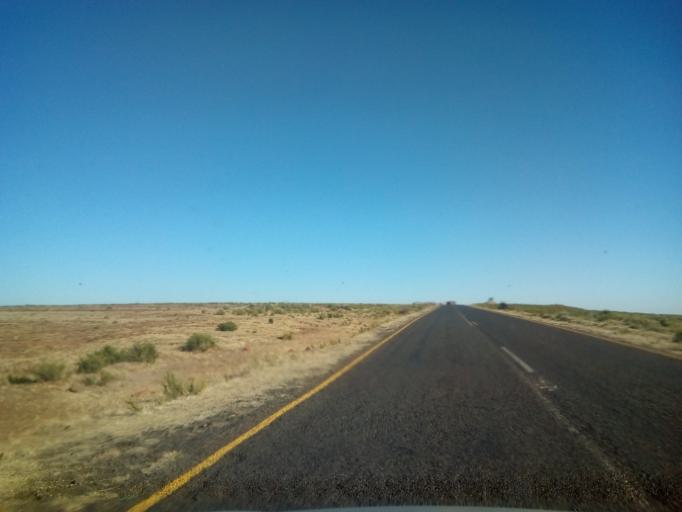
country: LS
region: Berea
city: Teyateyaneng
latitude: -29.2558
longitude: 27.7461
